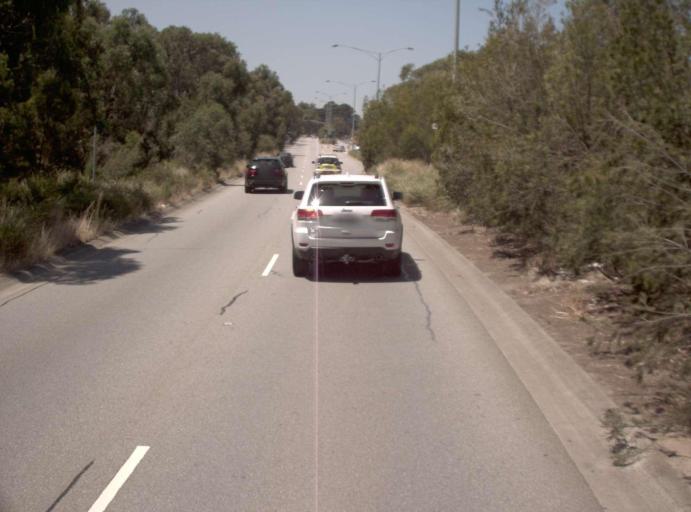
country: AU
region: Victoria
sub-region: Knox
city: Rowville
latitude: -37.9283
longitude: 145.2388
